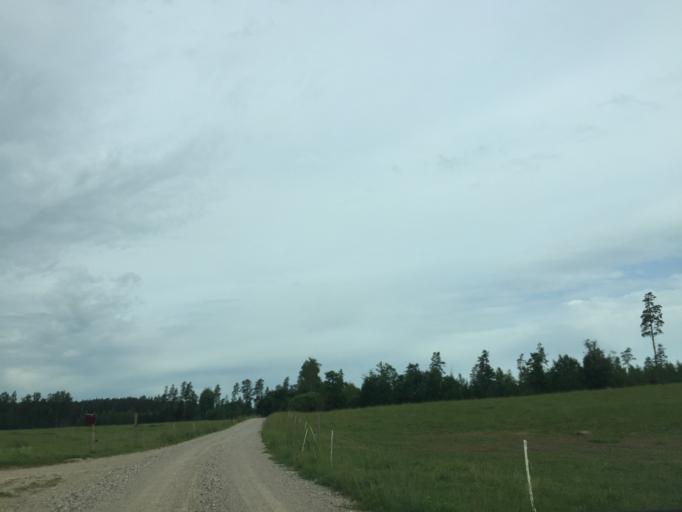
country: LV
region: Tukuma Rajons
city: Tukums
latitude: 57.0420
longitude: 23.1567
